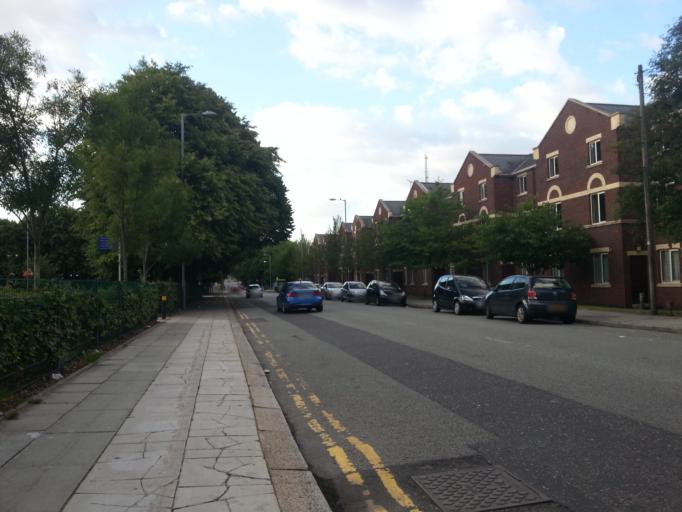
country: GB
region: England
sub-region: Liverpool
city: Liverpool
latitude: 53.4015
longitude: -2.9622
